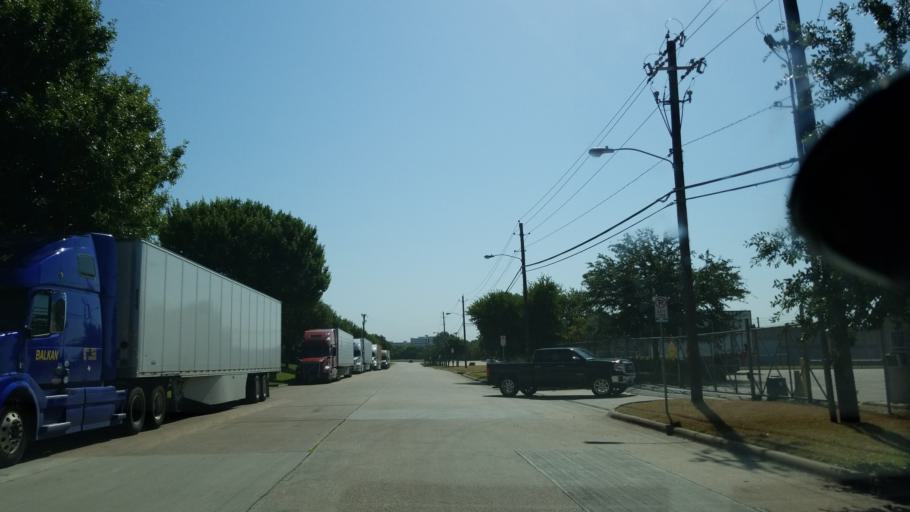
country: US
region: Texas
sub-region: Dallas County
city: Duncanville
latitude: 32.6957
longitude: -96.9129
